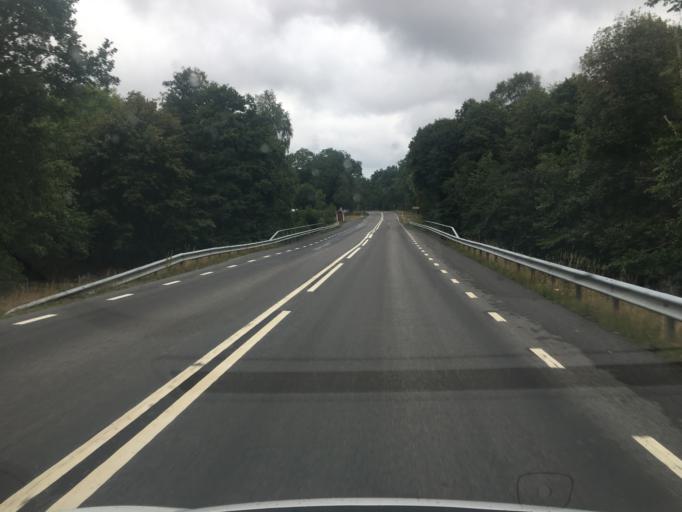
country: SE
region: Kronoberg
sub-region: Ljungby Kommun
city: Lagan
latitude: 57.0319
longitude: 14.0266
